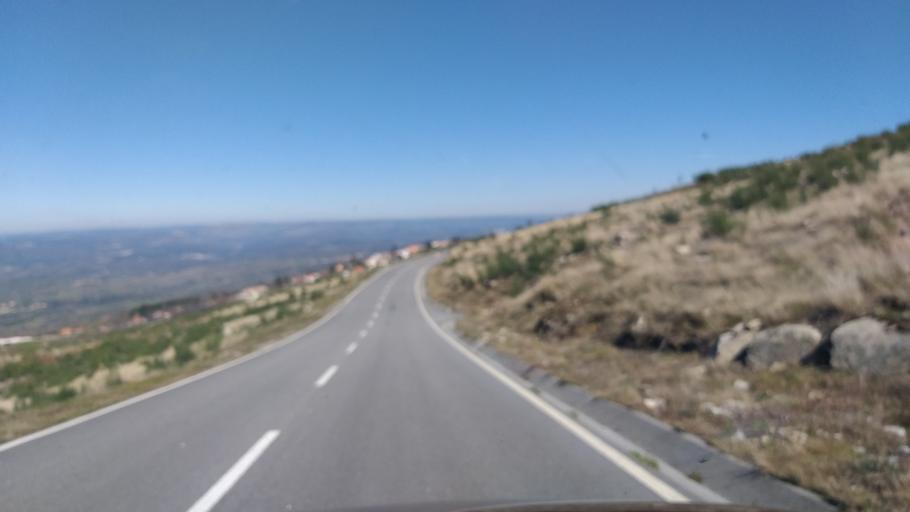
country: PT
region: Guarda
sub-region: Manteigas
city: Manteigas
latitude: 40.4977
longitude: -7.5243
